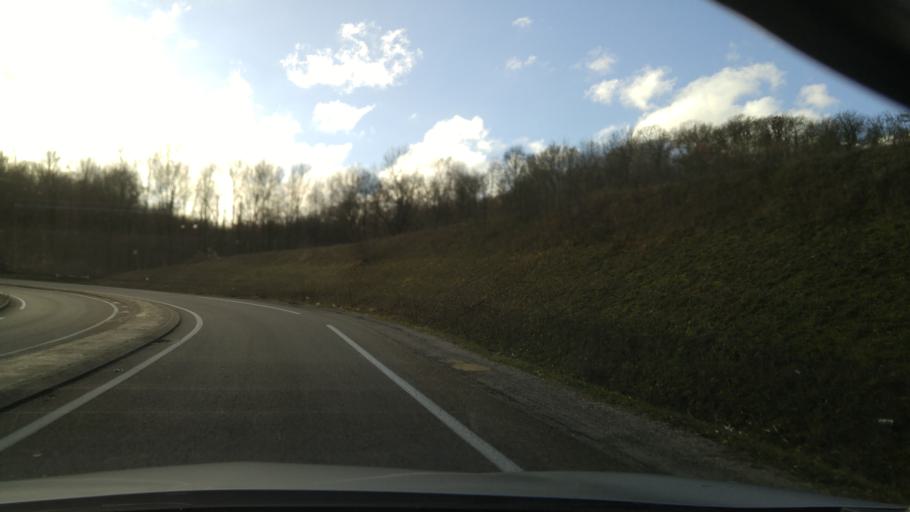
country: FR
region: Rhone-Alpes
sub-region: Departement de l'Isere
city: Roche
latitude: 45.6029
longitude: 5.1596
